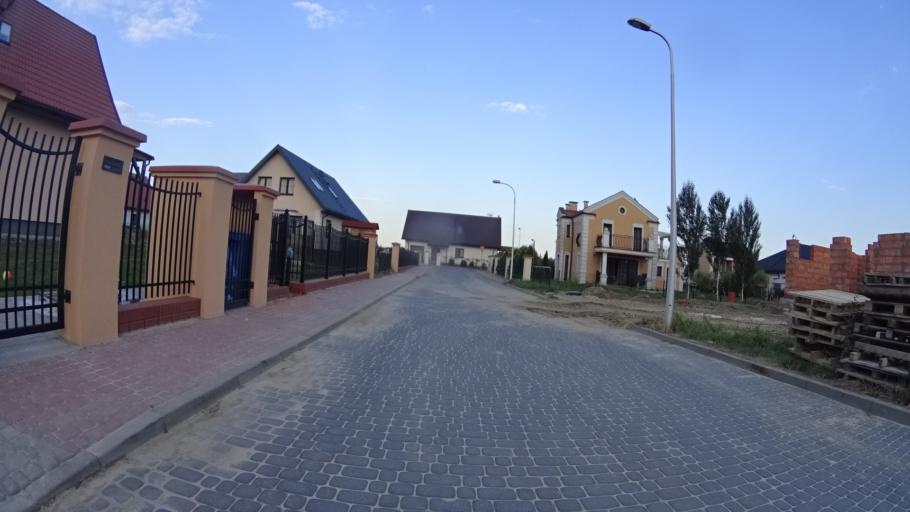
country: PL
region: Masovian Voivodeship
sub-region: Powiat warszawski zachodni
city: Ozarow Mazowiecki
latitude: 52.2333
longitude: 20.7720
